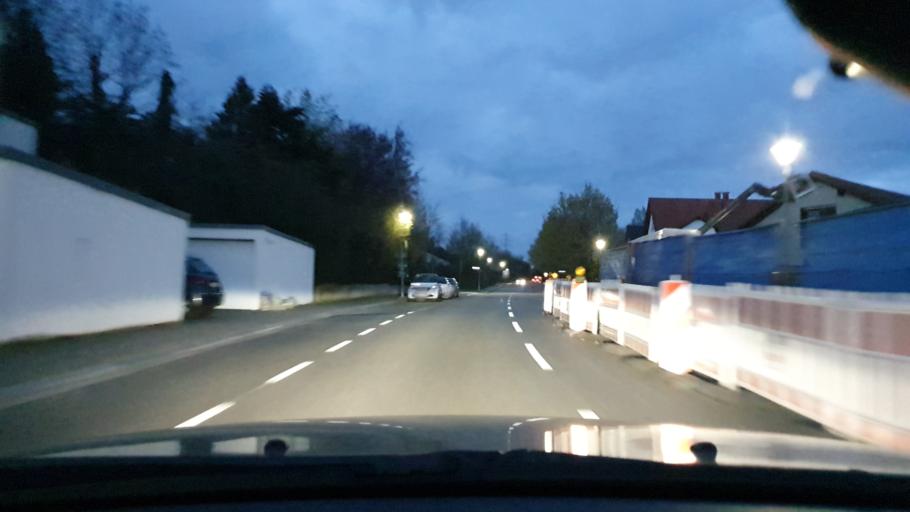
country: DE
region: Rheinland-Pfalz
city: Kaiserslautern
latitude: 49.4549
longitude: 7.7780
